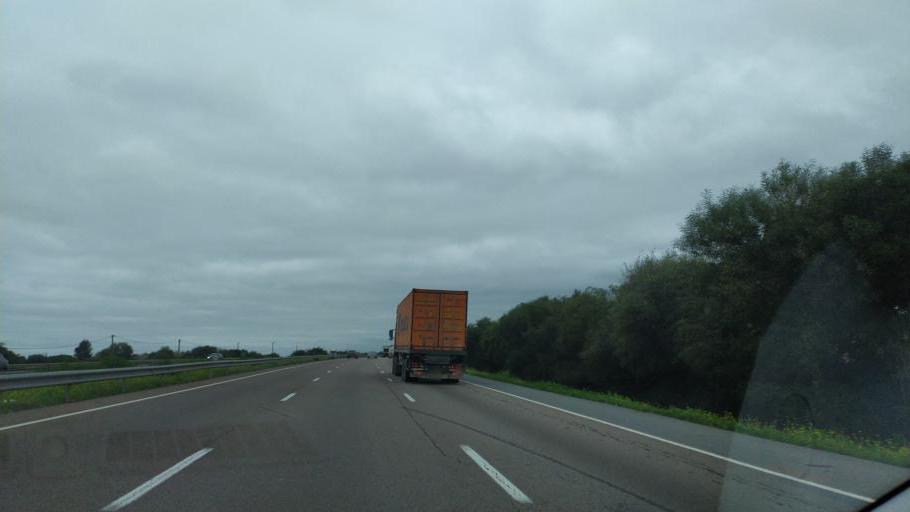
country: MA
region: Rabat-Sale-Zemmour-Zaer
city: Skhirat
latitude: 33.8515
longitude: -7.0687
